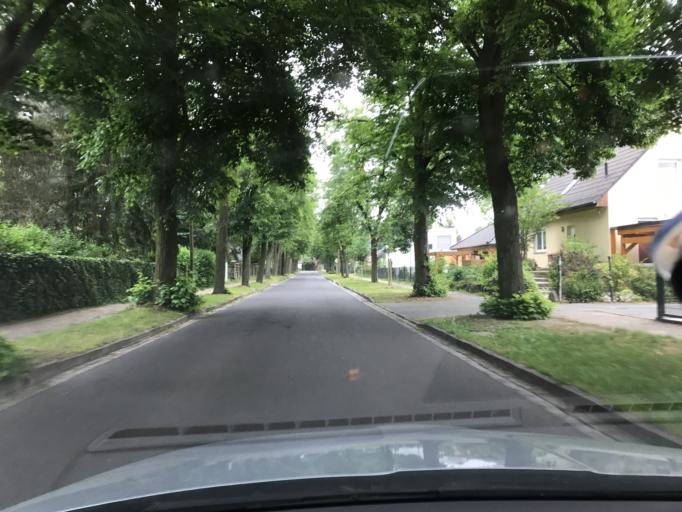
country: DE
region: Brandenburg
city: Falkensee
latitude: 52.5681
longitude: 13.0764
